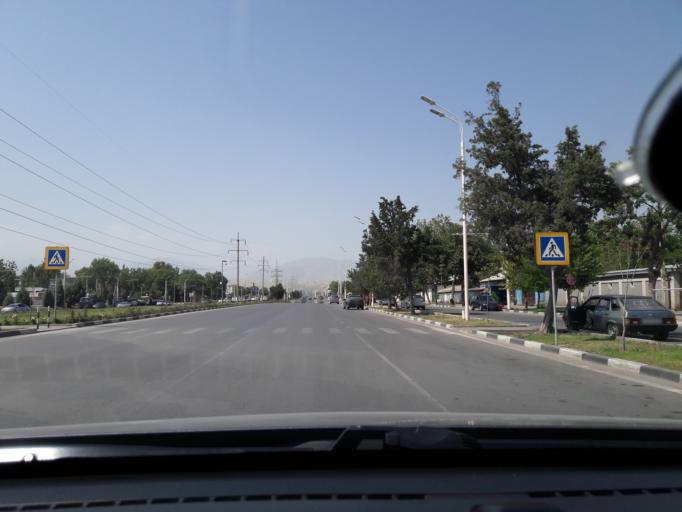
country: TJ
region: Dushanbe
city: Dushanbe
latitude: 38.5415
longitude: 68.7414
